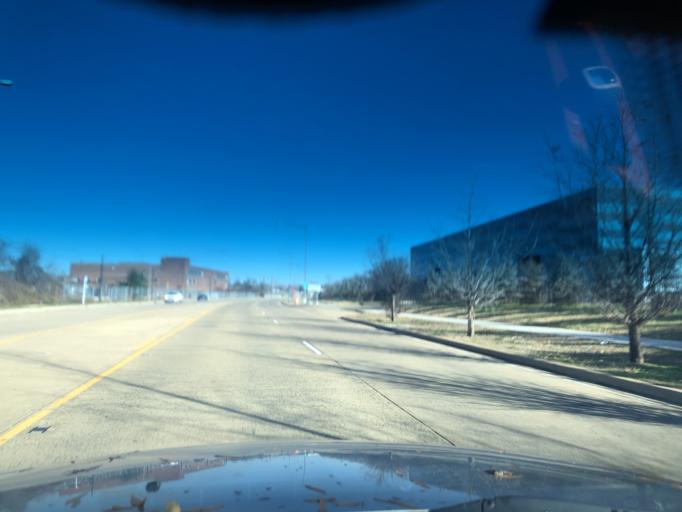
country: US
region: Maryland
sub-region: Prince George's County
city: Glassmanor
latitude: 38.8573
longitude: -77.0049
